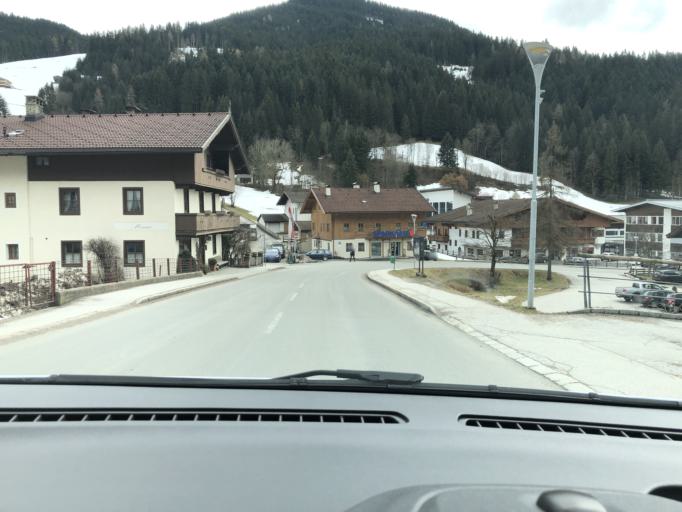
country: AT
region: Tyrol
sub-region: Politischer Bezirk Kufstein
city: Wildschoenau
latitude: 47.4435
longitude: 12.0488
